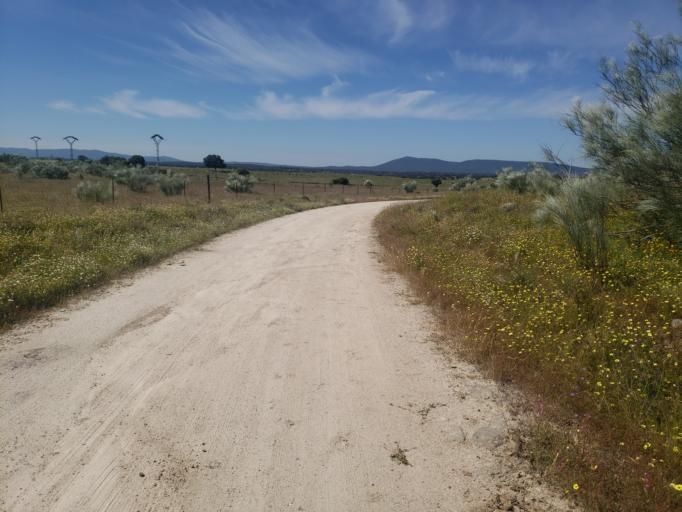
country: ES
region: Extremadura
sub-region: Provincia de Caceres
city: Malpartida de Caceres
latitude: 39.4177
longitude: -6.5006
